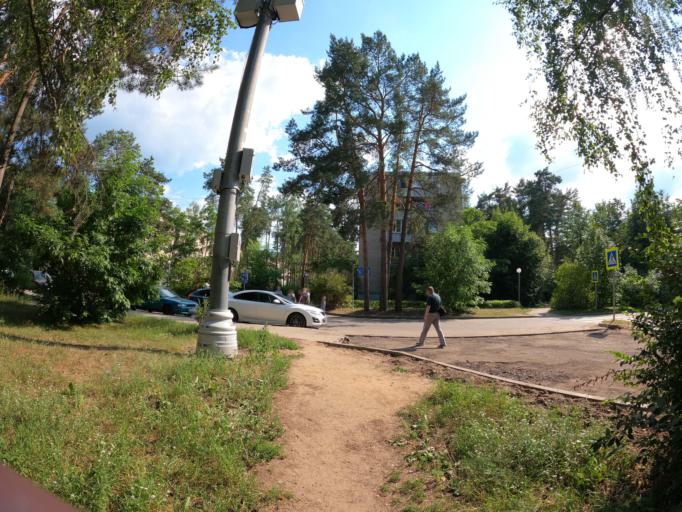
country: RU
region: Moskovskaya
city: Protvino
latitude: 54.8668
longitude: 37.2182
